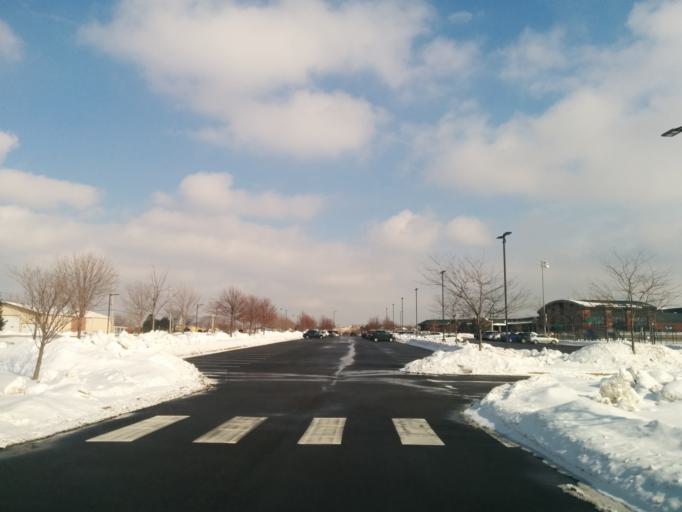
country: US
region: Illinois
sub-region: Cook County
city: Orland Hills
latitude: 41.5797
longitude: -87.8177
